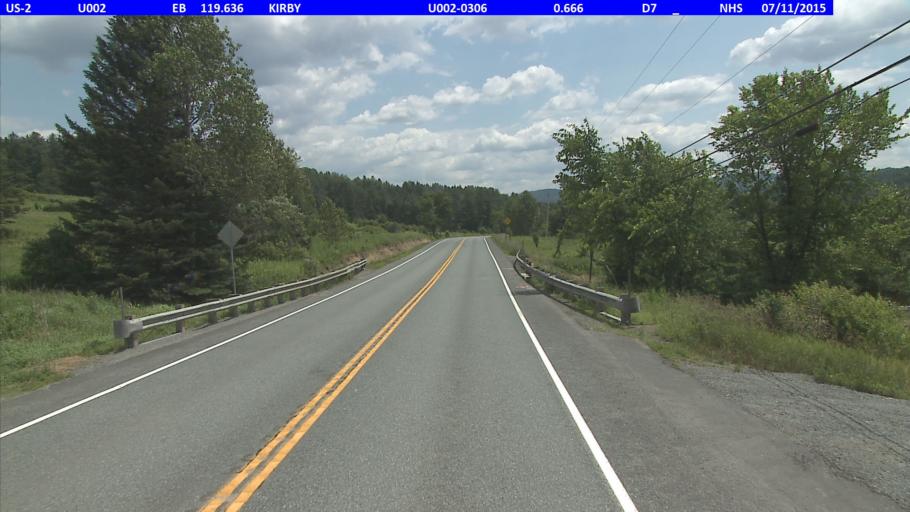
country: US
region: Vermont
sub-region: Caledonia County
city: St Johnsbury
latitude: 44.4501
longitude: -71.9248
